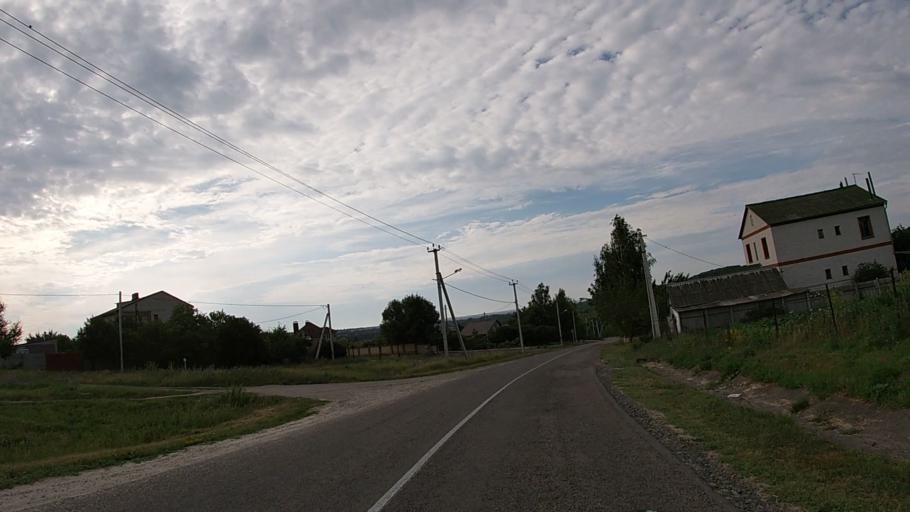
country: RU
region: Belgorod
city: Severnyy
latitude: 50.7141
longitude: 36.5948
